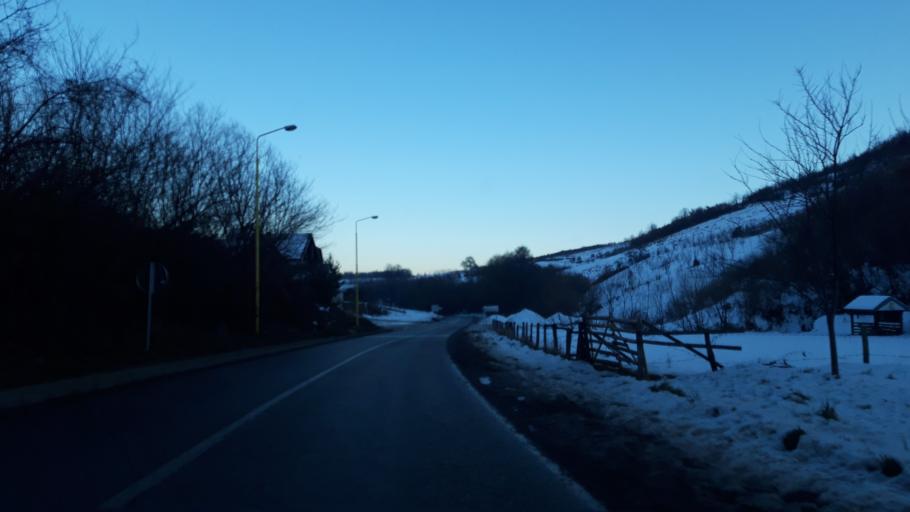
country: BA
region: Republika Srpska
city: Vlasenica
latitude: 44.1801
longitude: 18.9530
